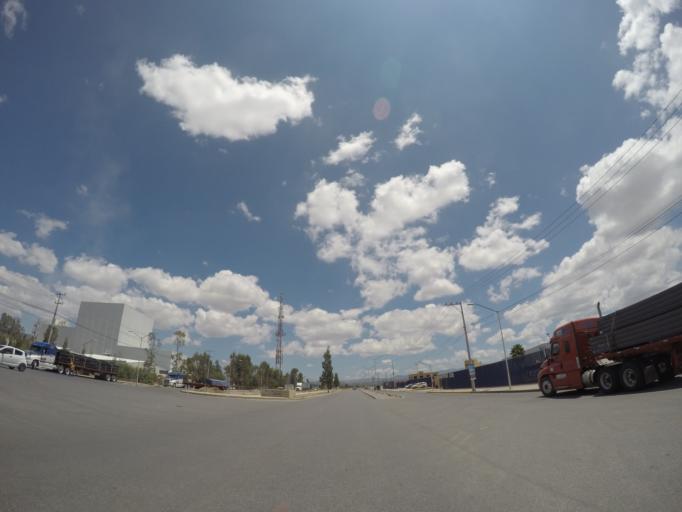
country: MX
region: San Luis Potosi
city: La Pila
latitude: 22.0505
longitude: -100.8664
